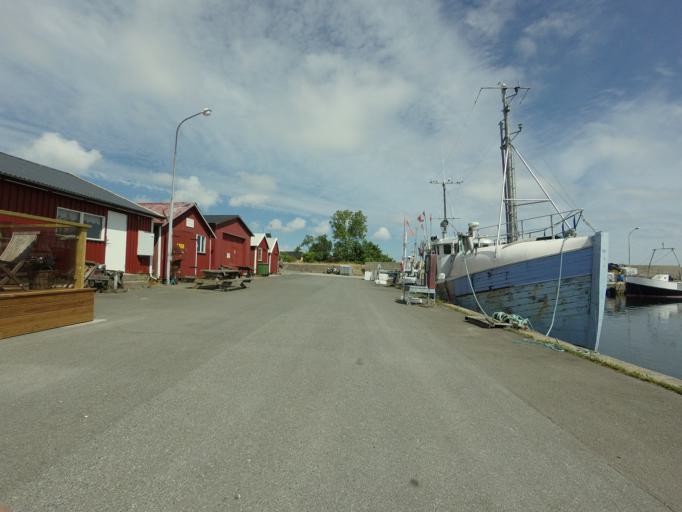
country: SE
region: Skane
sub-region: Simrishamns Kommun
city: Simrishamn
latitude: 55.5137
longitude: 14.3484
